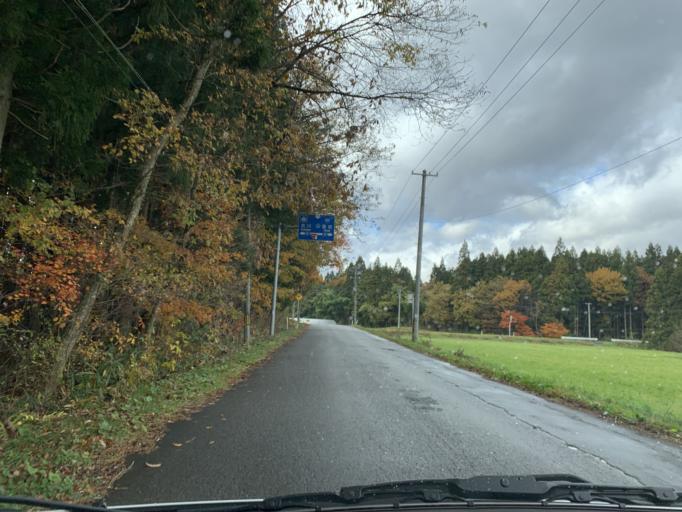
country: JP
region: Iwate
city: Mizusawa
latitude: 39.1042
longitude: 140.9886
